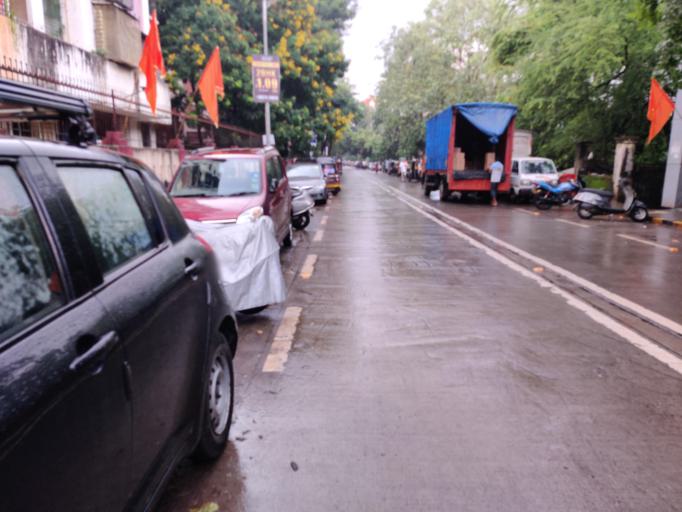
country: IN
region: Maharashtra
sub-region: Mumbai Suburban
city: Borivli
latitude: 19.2488
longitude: 72.8549
